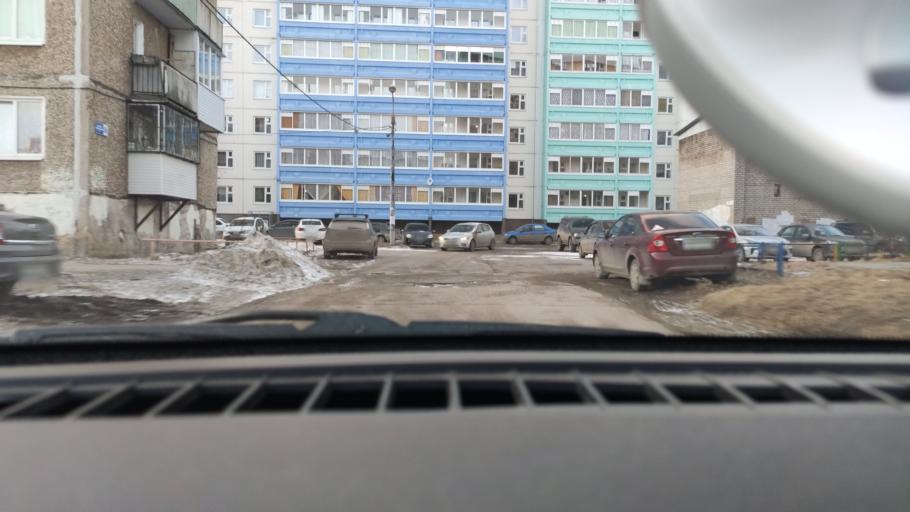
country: RU
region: Perm
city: Perm
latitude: 58.0863
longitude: 56.4083
